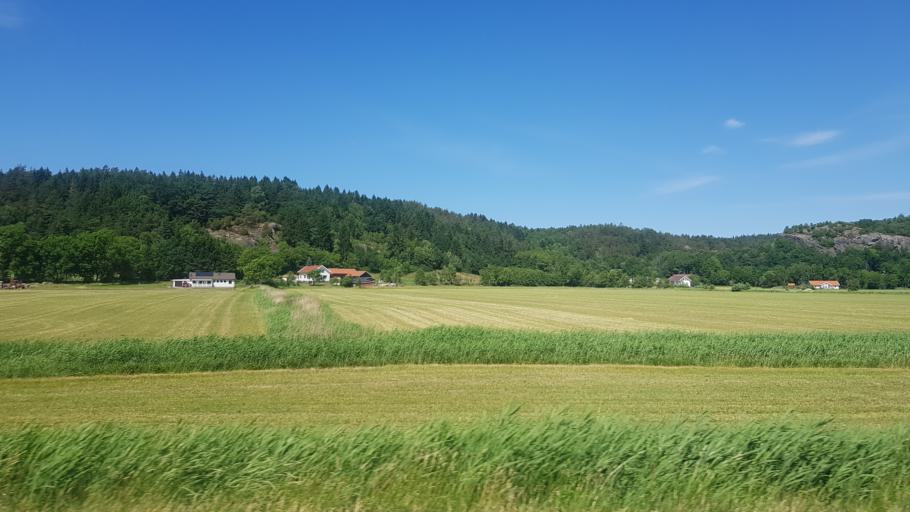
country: SE
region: Vaestra Goetaland
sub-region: Tjorns Kommun
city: Skaerhamn
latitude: 58.0231
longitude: 11.6391
